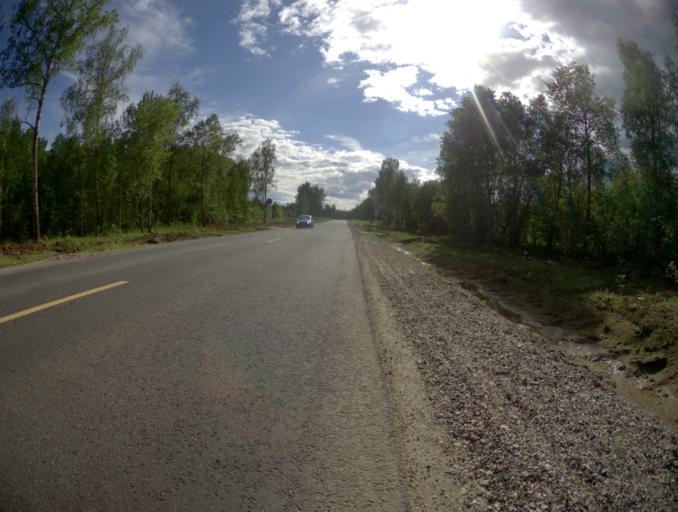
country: RU
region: Ivanovo
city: Kitovo
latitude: 56.8237
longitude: 41.2773
